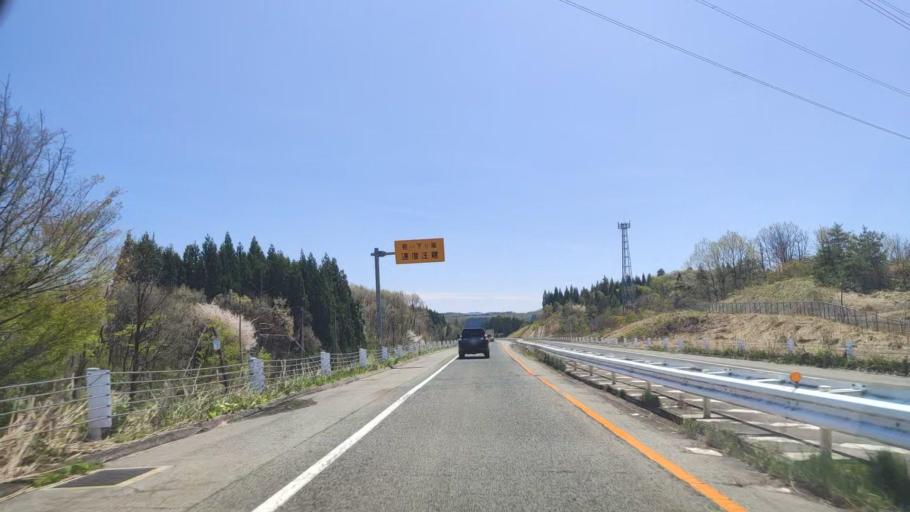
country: JP
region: Yamagata
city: Shinjo
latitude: 38.7163
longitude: 140.3090
